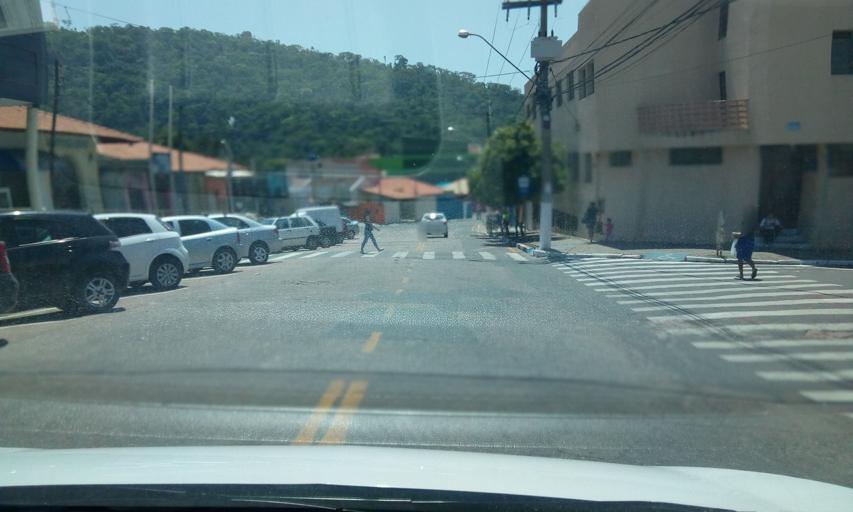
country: BR
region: Sao Paulo
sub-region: Itupeva
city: Itupeva
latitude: -23.1536
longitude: -47.0586
